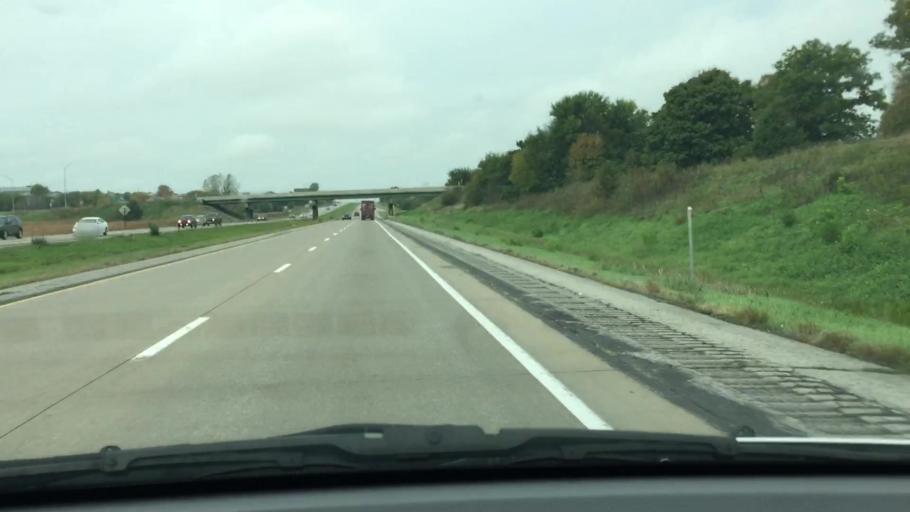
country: US
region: Iowa
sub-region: Johnson County
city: Iowa City
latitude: 41.6708
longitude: -91.4431
